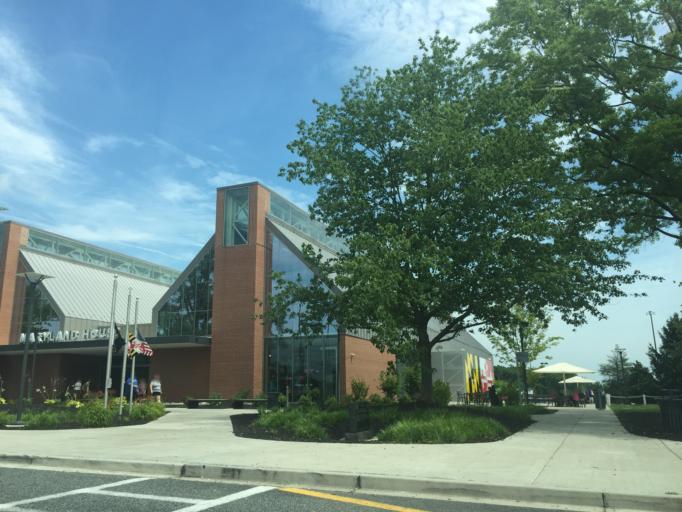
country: US
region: Maryland
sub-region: Harford County
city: Riverside
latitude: 39.4968
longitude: -76.2323
